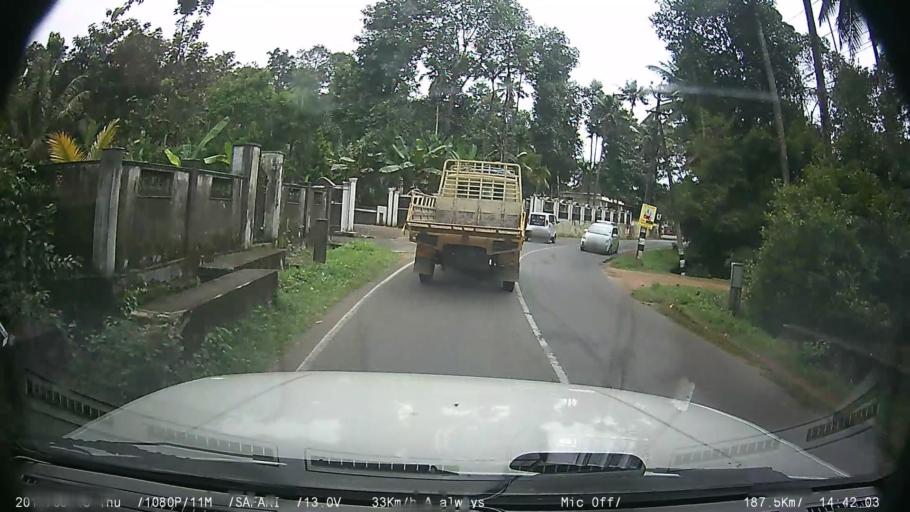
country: IN
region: Kerala
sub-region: Ernakulam
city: Muvattupula
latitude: 10.0073
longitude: 76.6052
